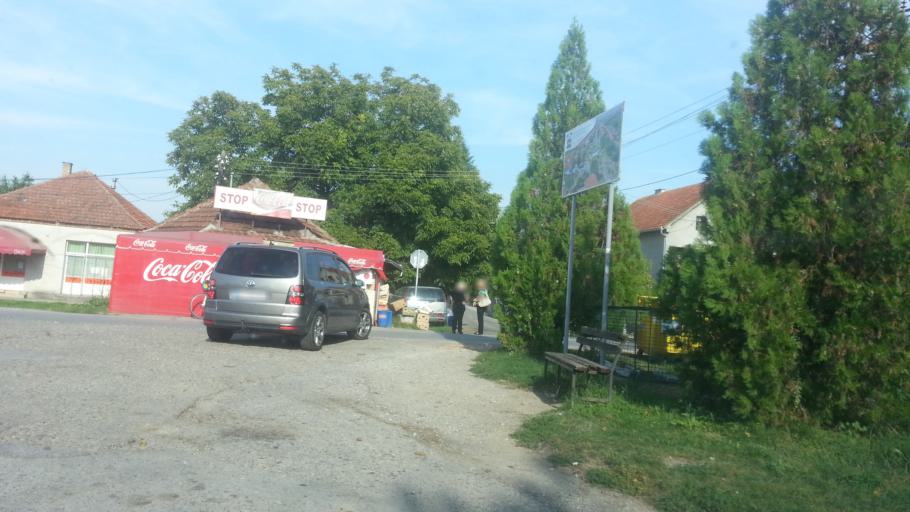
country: RS
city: Novi Banovci
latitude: 44.9505
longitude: 20.2828
